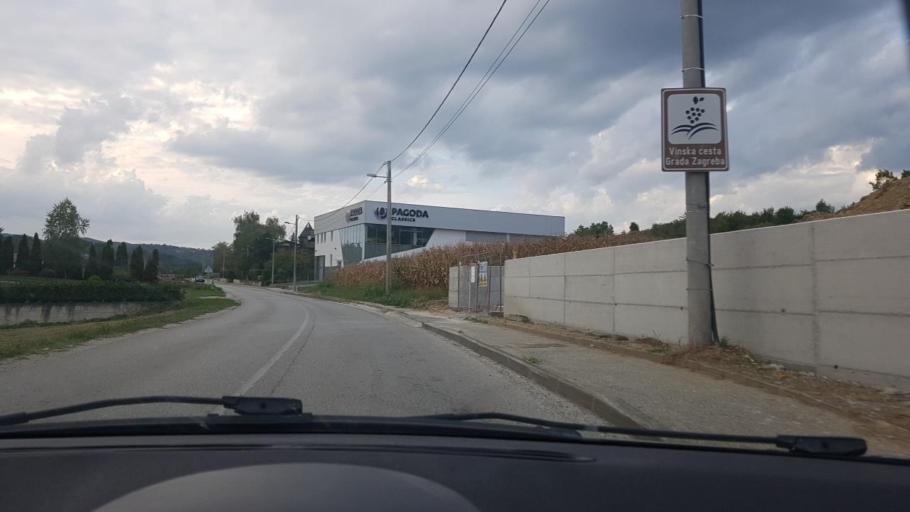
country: HR
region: Grad Zagreb
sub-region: Sesvete
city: Sesvete
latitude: 45.8993
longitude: 16.1655
